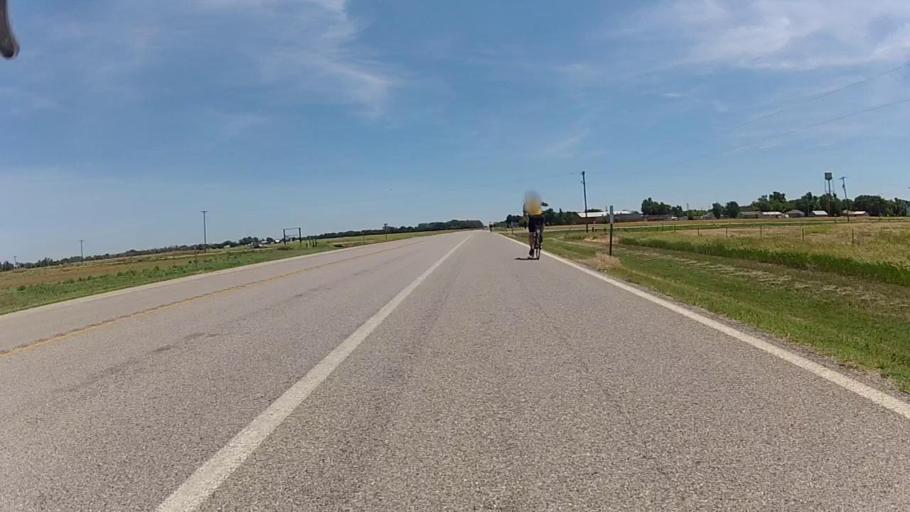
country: US
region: Kansas
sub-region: Barber County
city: Medicine Lodge
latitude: 37.2536
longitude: -98.4232
